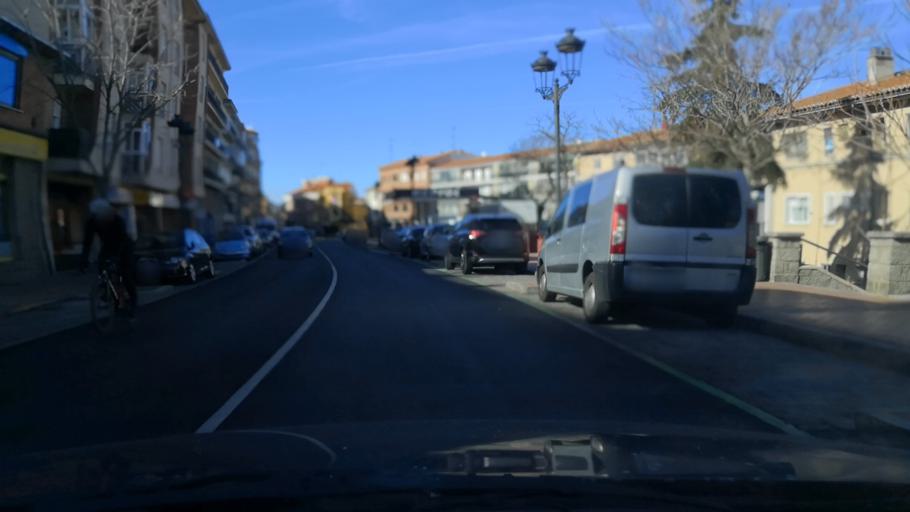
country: ES
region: Castille and Leon
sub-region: Provincia de Avila
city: Avila
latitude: 40.6576
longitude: -4.6908
